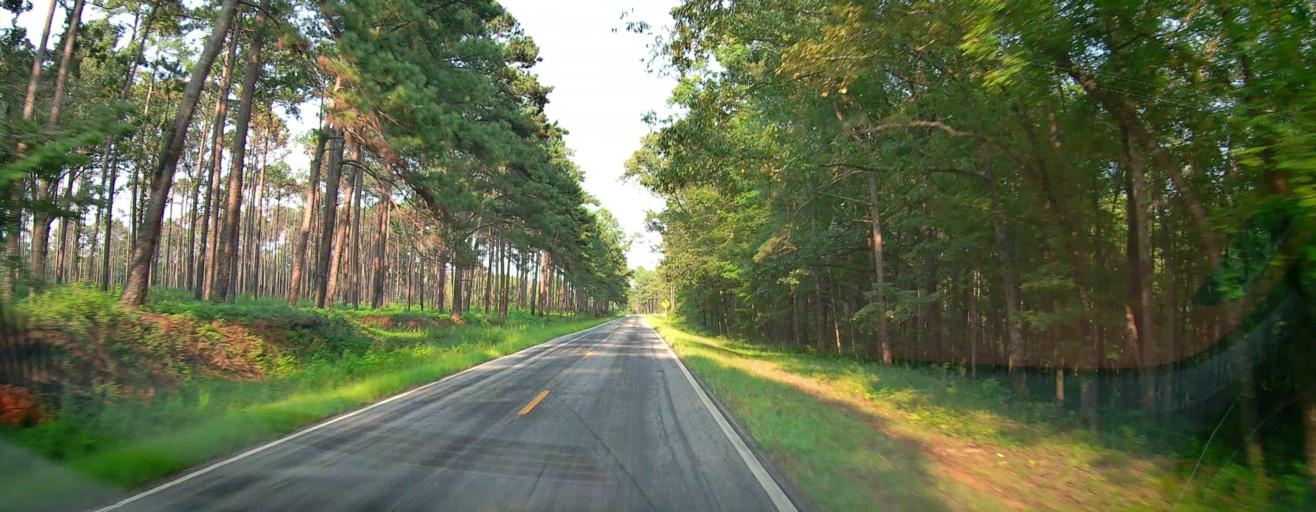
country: US
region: Georgia
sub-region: Jones County
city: Gray
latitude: 33.0966
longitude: -83.6853
